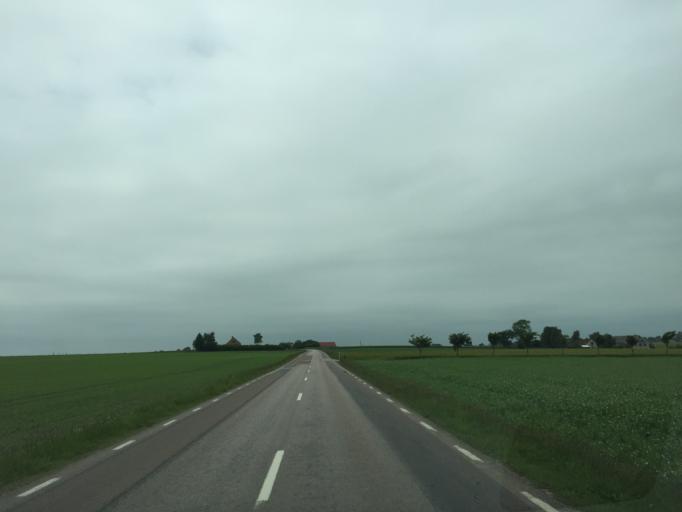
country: SE
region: Skane
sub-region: Ystads Kommun
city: Kopingebro
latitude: 55.4289
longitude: 14.0883
